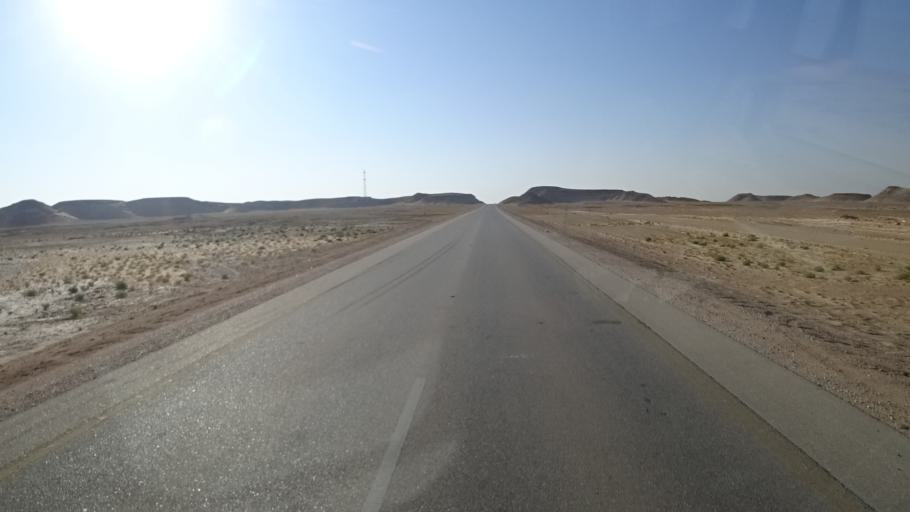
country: OM
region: Zufar
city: Salalah
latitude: 17.6410
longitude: 53.8619
